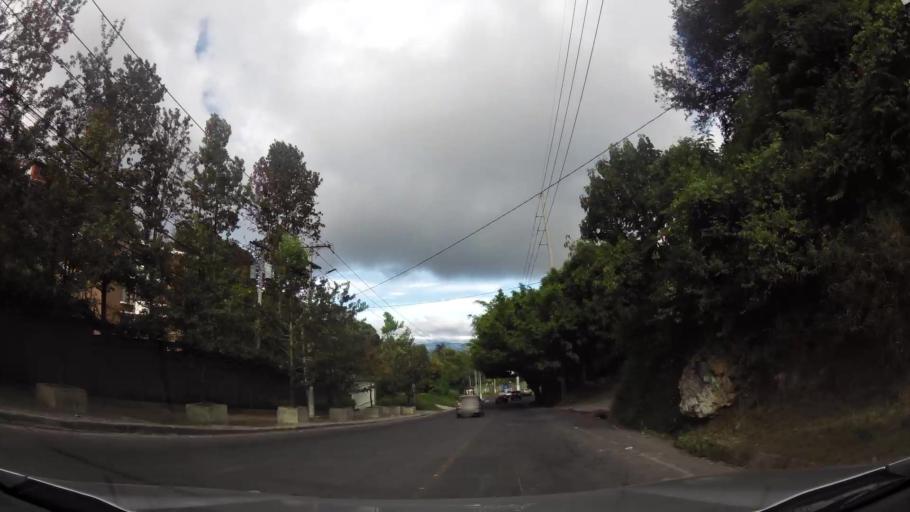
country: GT
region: Guatemala
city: Santa Catarina Pinula
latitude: 14.5676
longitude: -90.4837
